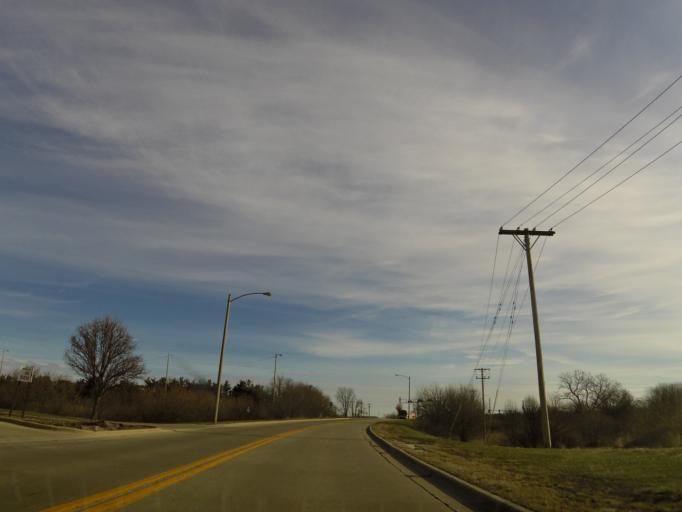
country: US
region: Illinois
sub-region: McLean County
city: Normal
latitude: 40.5080
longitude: -89.0362
